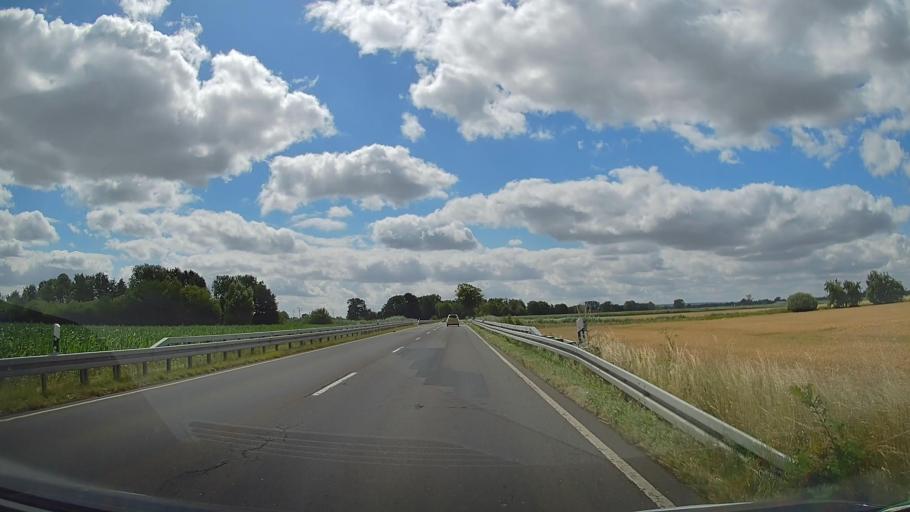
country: DE
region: Lower Saxony
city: Lembruch
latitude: 52.5472
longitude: 8.3716
